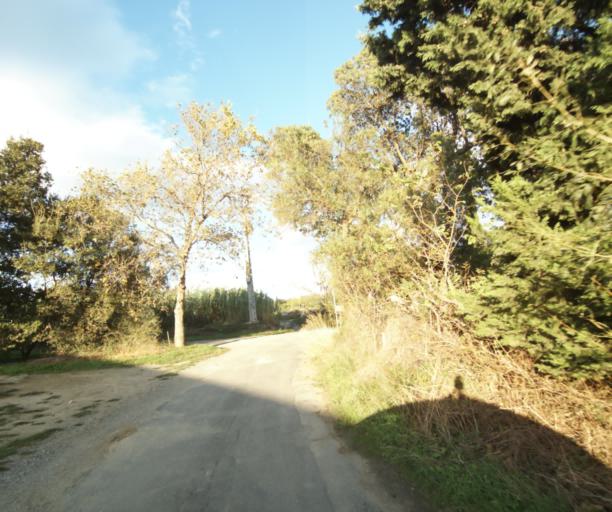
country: FR
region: Languedoc-Roussillon
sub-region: Departement des Pyrenees-Orientales
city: Latour-Bas-Elne
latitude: 42.5788
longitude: 3.0126
